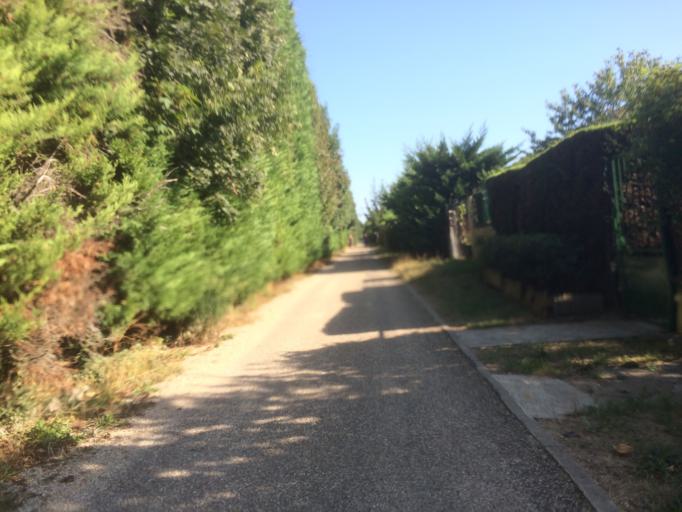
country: FR
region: Ile-de-France
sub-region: Departement de l'Essonne
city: Epinay-sur-Orge
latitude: 48.6806
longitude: 2.3239
